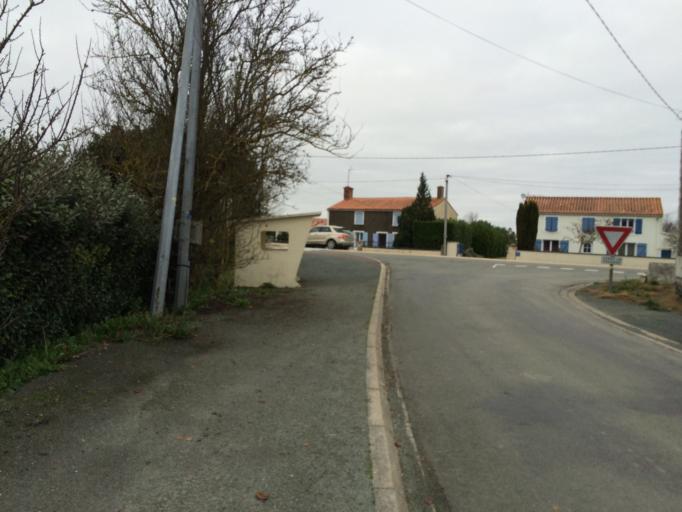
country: FR
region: Pays de la Loire
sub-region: Departement de la Vendee
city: Chaille-les-Marais
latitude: 46.3778
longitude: -1.0139
